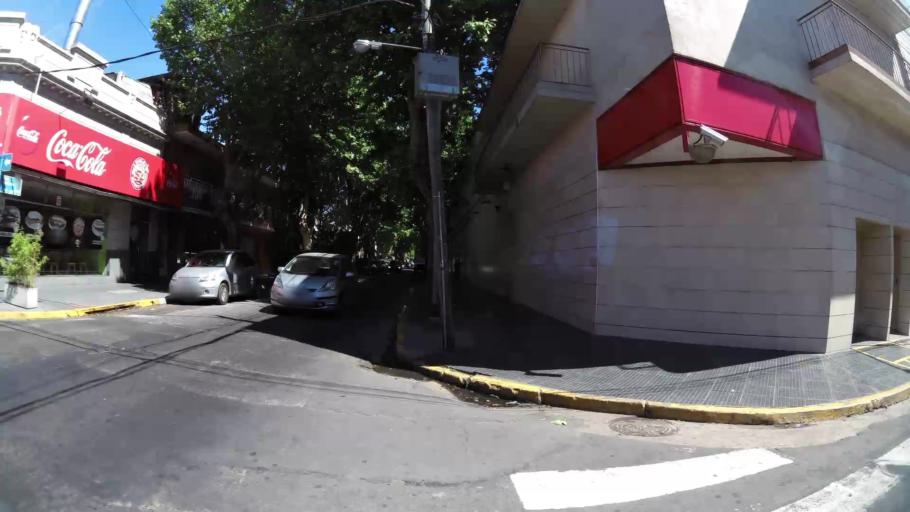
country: AR
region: Buenos Aires
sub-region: Partido de General San Martin
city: General San Martin
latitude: -34.5790
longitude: -58.5410
